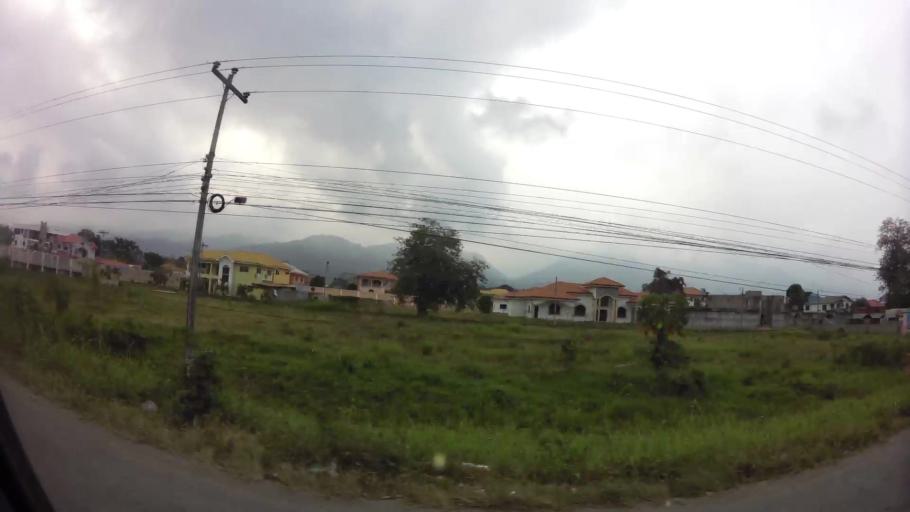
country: HN
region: Yoro
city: El Progreso
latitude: 15.4377
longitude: -87.7934
